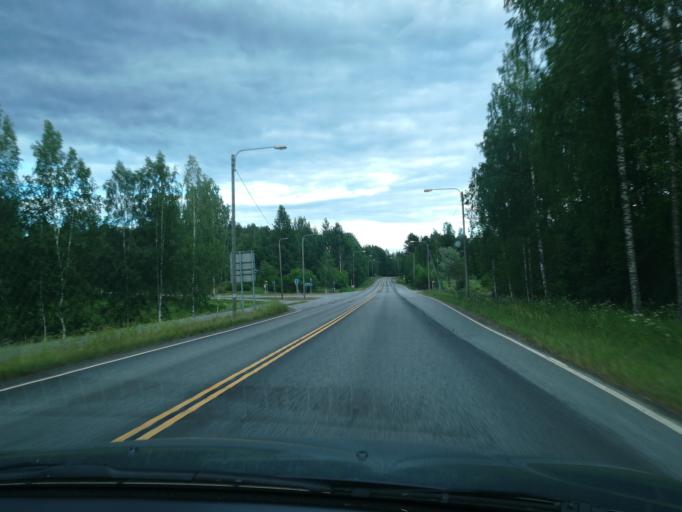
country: FI
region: Southern Savonia
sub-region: Mikkeli
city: Mikkeli
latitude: 61.5882
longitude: 27.6238
